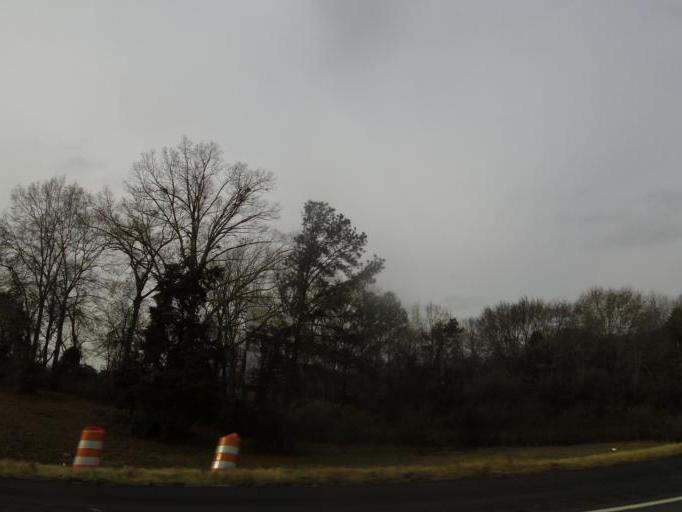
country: US
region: Alabama
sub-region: Elmore County
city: Millbrook
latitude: 32.4684
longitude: -86.3933
